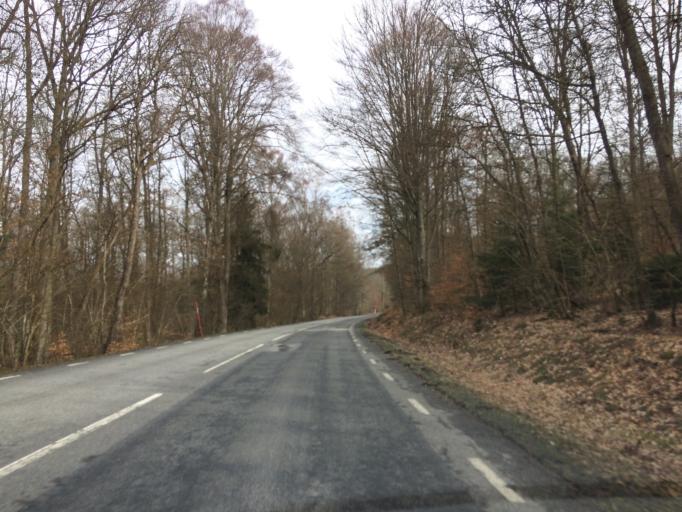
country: SE
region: Skane
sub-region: Osby Kommun
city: Lonsboda
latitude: 56.3006
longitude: 14.3013
